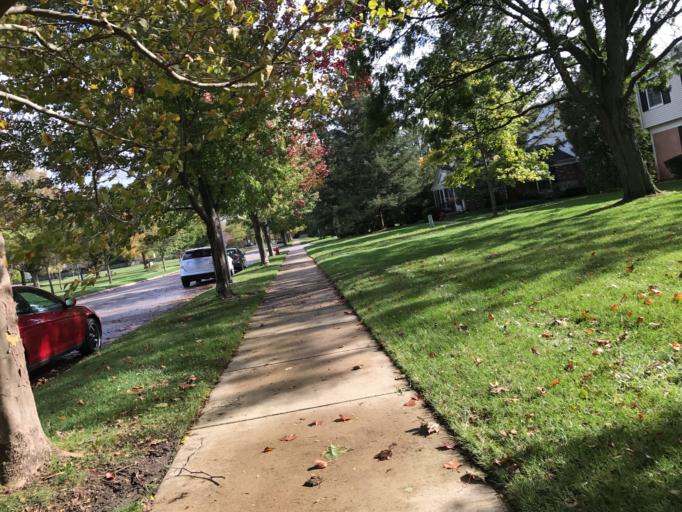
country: US
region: Michigan
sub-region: Washtenaw County
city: Ann Arbor
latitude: 42.2484
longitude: -83.7275
